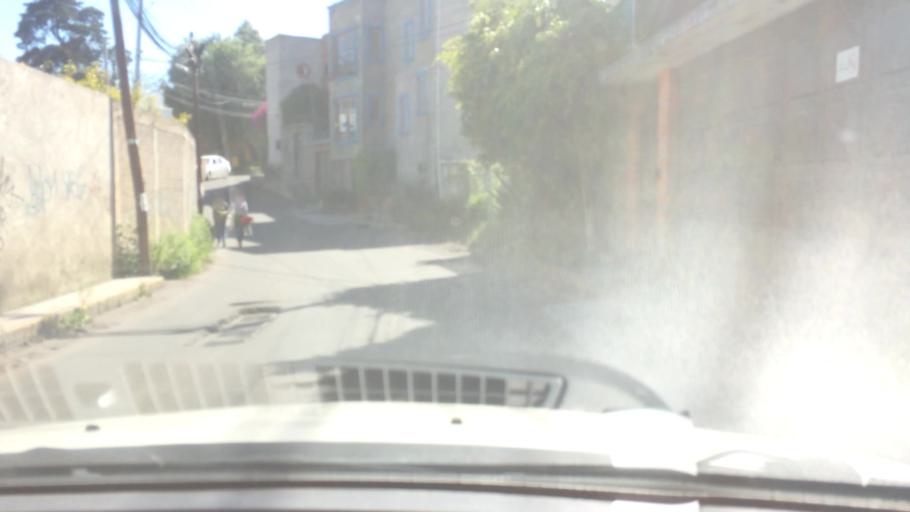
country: MX
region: Mexico City
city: Xochimilco
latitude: 19.2406
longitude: -99.1500
